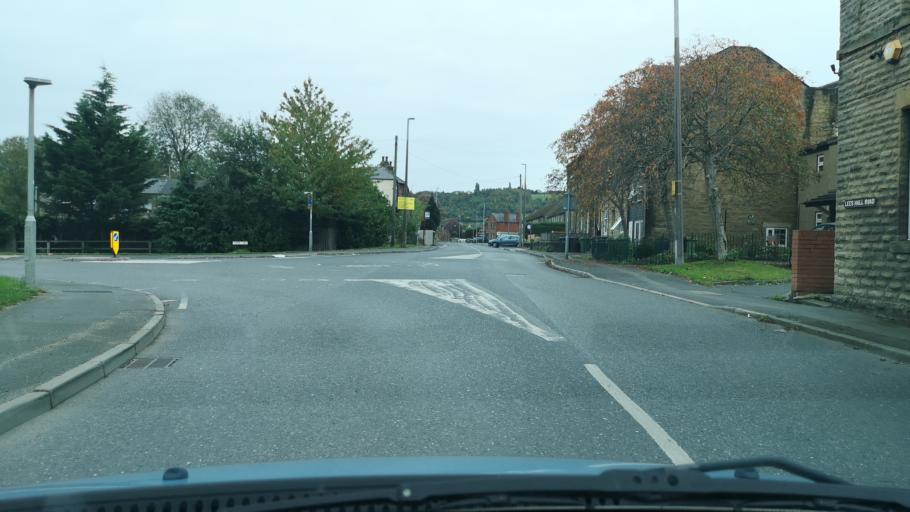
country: GB
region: England
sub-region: Kirklees
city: Dewsbury
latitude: 53.6735
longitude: -1.6458
